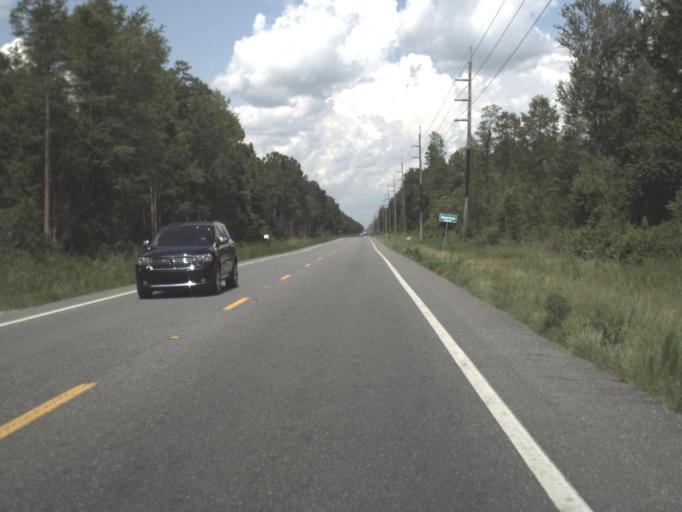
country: US
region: Florida
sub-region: Gilchrist County
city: Trenton
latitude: 29.6203
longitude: -82.7672
